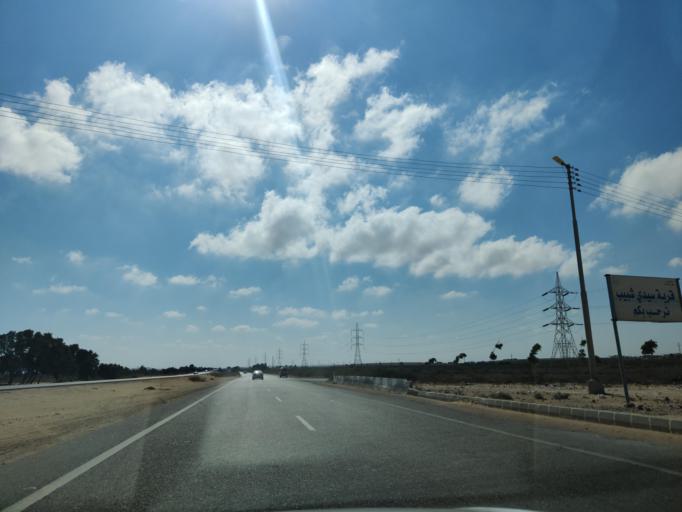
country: EG
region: Muhafazat Matruh
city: Al `Alamayn
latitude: 31.0542
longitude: 28.2904
